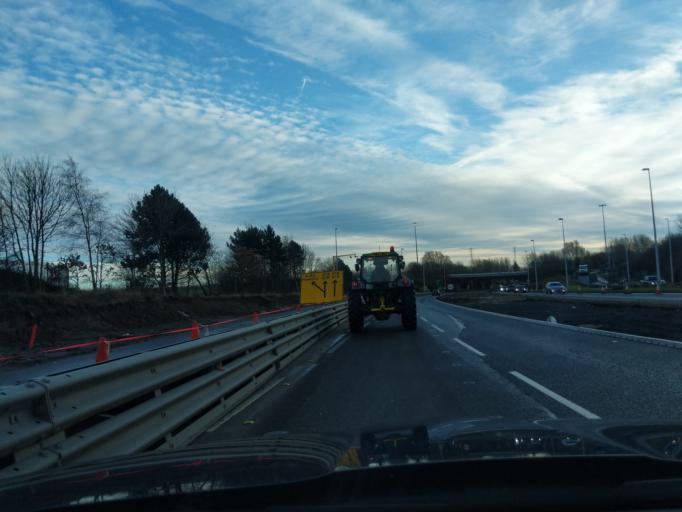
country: GB
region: England
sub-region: South Tyneside
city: Jarrow
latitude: 55.0018
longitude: -1.4883
